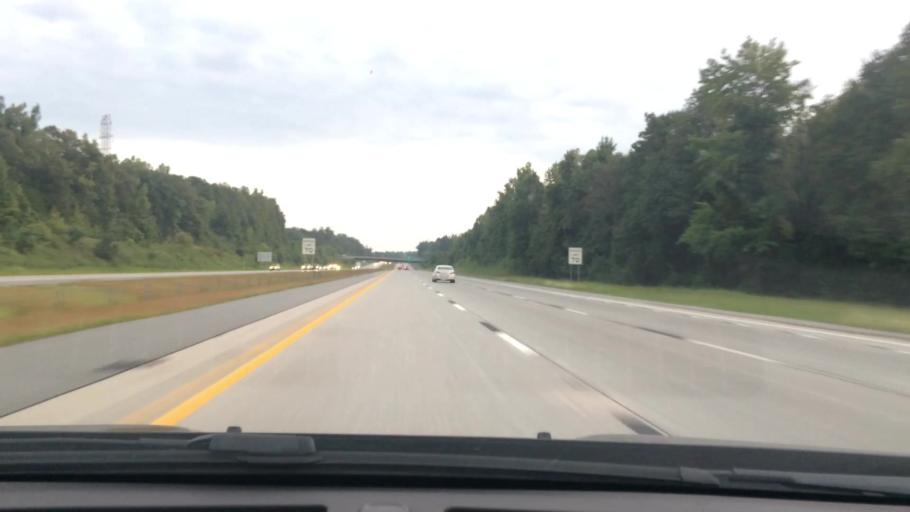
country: US
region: North Carolina
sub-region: Guilford County
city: Forest Oaks
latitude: 36.0184
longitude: -79.7339
